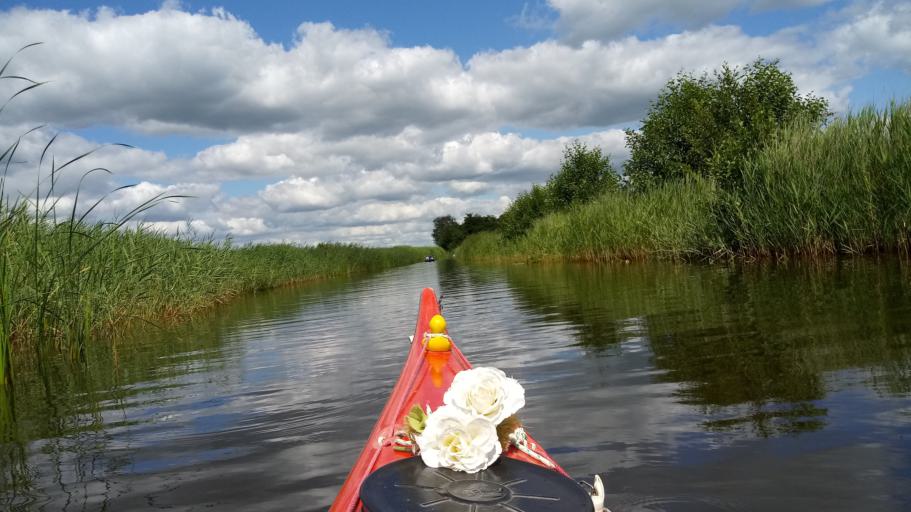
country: NL
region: Overijssel
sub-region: Gemeente Steenwijkerland
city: Wanneperveen
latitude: 52.7237
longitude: 6.1120
